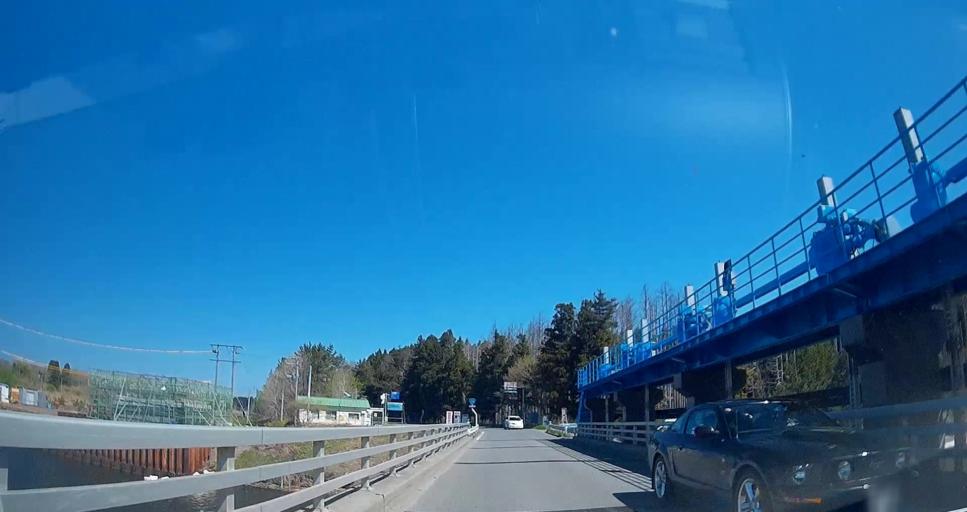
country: JP
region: Aomori
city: Misawa
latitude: 40.8443
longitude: 141.3833
